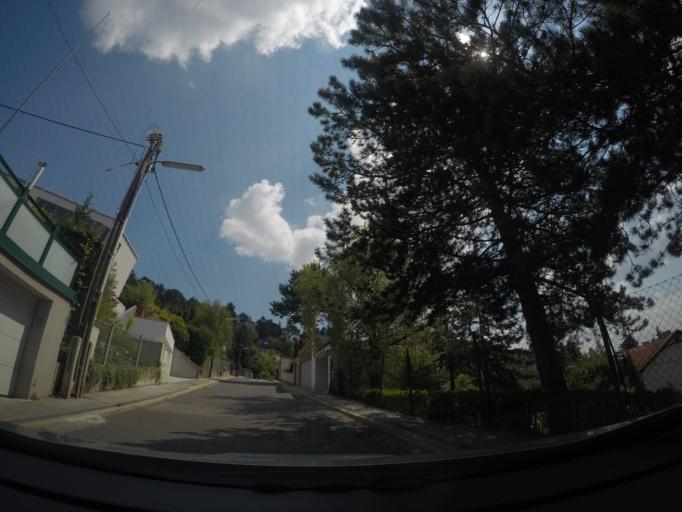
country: AT
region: Lower Austria
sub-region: Politischer Bezirk Wien-Umgebung
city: Purkersdorf
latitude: 48.2188
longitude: 16.2539
